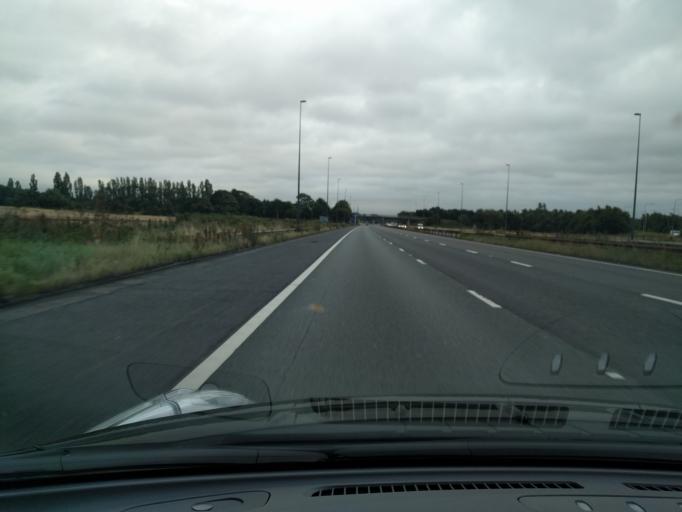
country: GB
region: England
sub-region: Warrington
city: Croft
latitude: 53.4322
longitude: -2.5671
